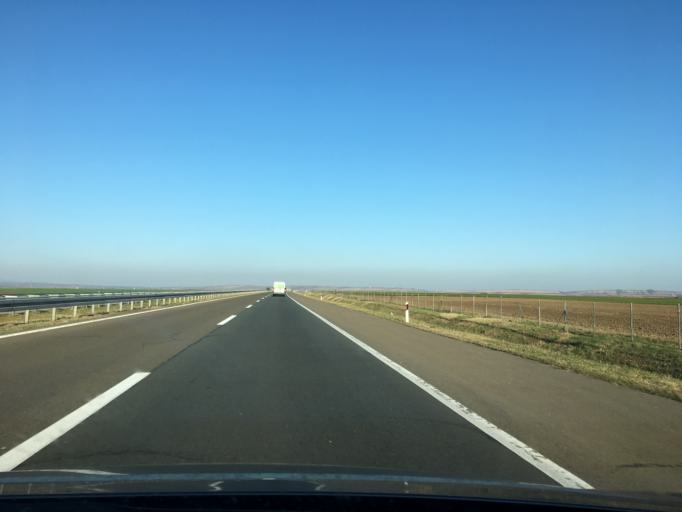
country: RS
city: Krcedin
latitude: 45.1041
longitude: 20.1095
